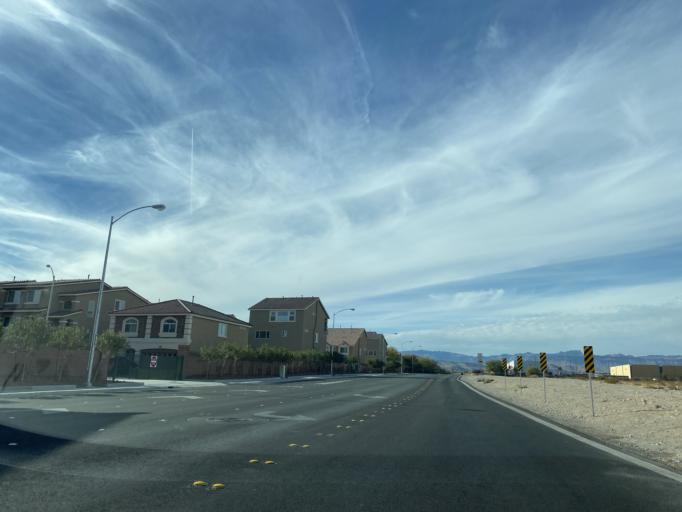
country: US
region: Nevada
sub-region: Clark County
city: Enterprise
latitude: 36.0620
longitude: -115.2249
